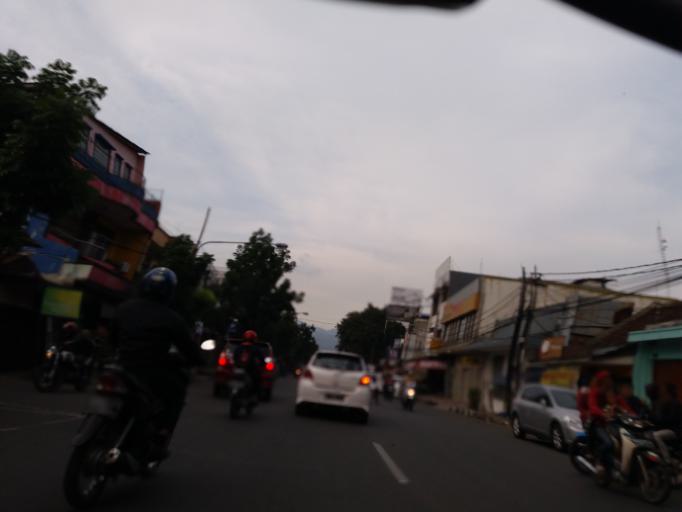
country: ID
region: West Java
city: Bandung
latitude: -6.9065
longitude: 107.6474
